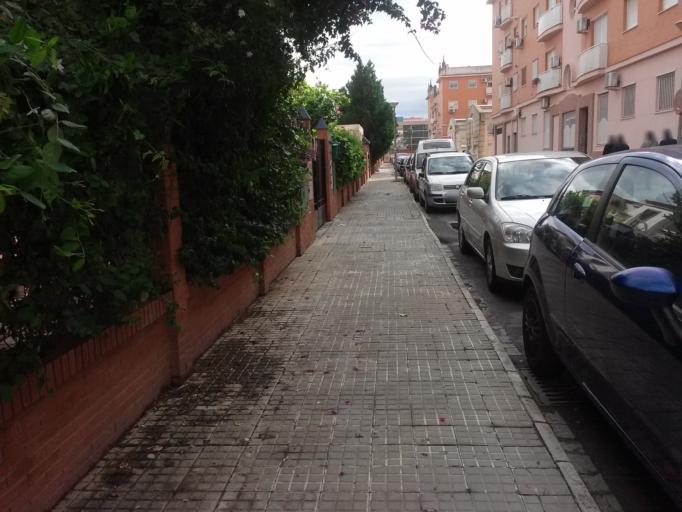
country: ES
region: Andalusia
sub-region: Provincia de Sevilla
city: La Algaba
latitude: 37.4275
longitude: -5.9860
